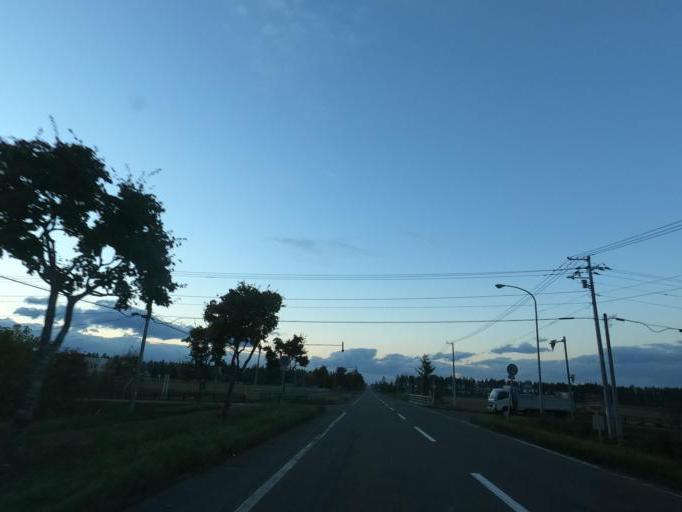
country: JP
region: Hokkaido
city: Obihiro
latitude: 42.6417
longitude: 143.2025
